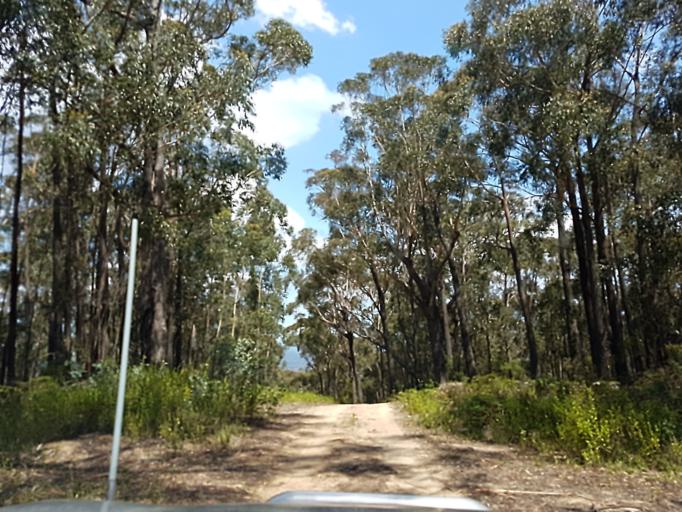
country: AU
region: Victoria
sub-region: East Gippsland
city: Lakes Entrance
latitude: -37.3971
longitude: 148.2979
